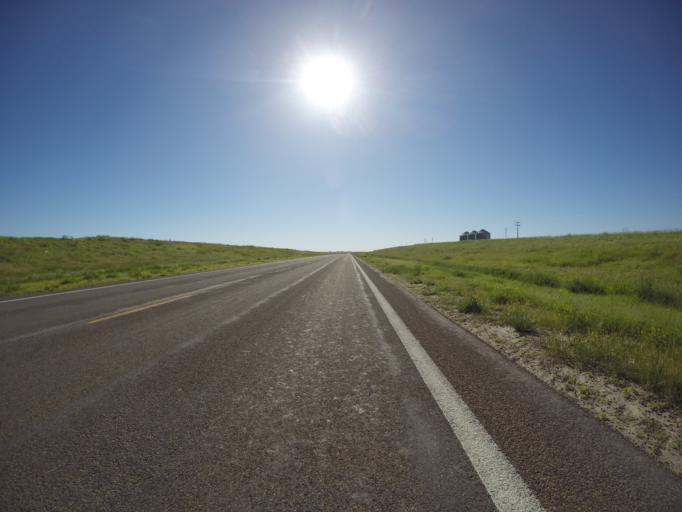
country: US
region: Kansas
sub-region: Norton County
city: Norton
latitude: 39.8281
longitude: -100.0334
